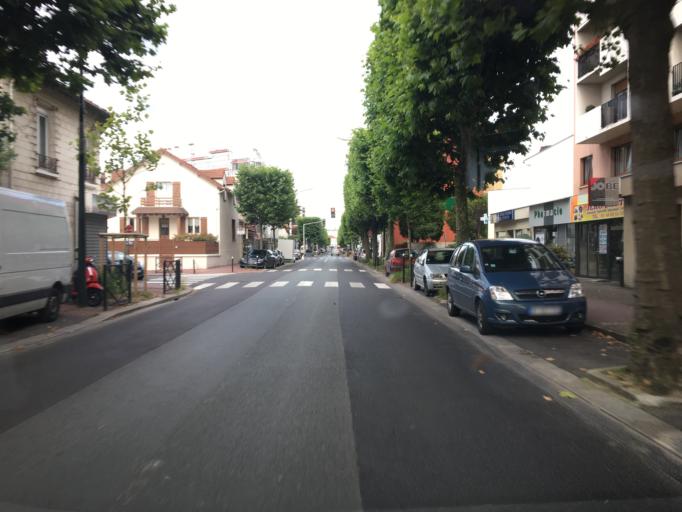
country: FR
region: Ile-de-France
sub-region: Departement du Val-de-Marne
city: Saint-Maur-des-Fosses
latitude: 48.7979
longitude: 2.4971
